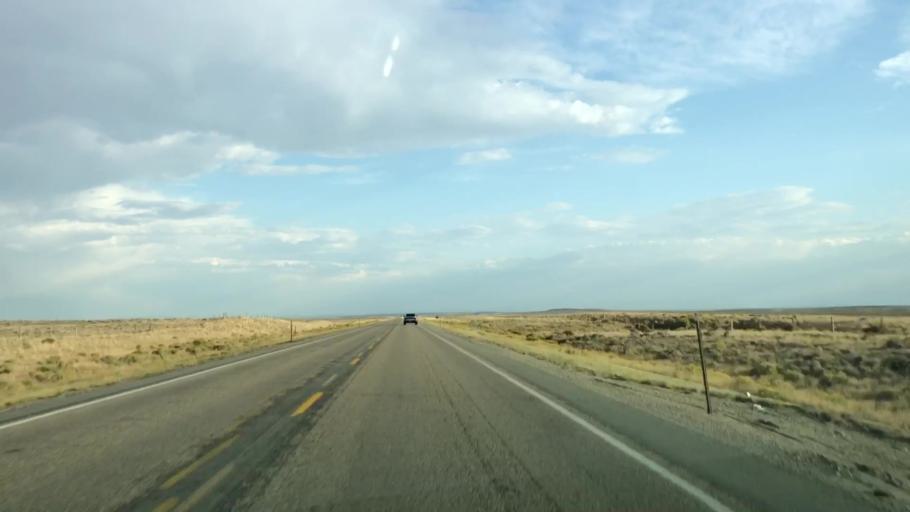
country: US
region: Wyoming
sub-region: Sublette County
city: Pinedale
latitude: 42.4066
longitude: -109.5499
